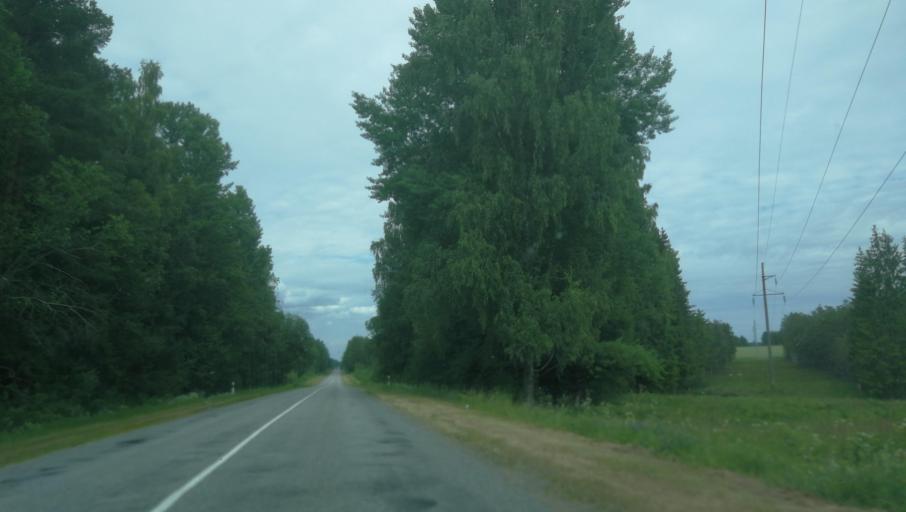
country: LV
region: Valmieras Rajons
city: Valmiera
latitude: 57.6975
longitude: 25.4284
